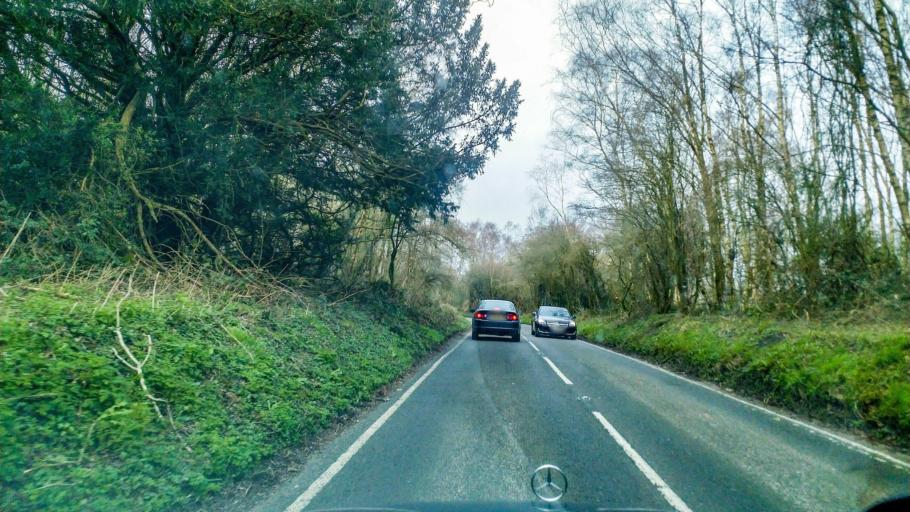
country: GB
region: England
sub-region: Surrey
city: Chilworth
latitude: 51.2381
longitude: -0.5138
